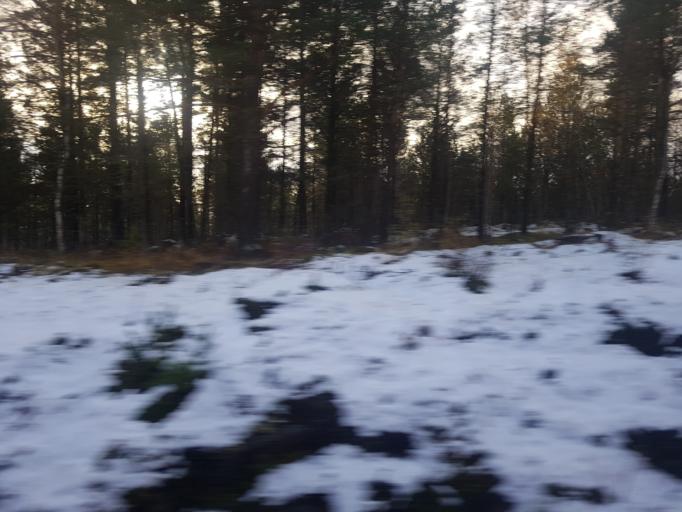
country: NO
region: Sor-Trondelag
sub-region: Oppdal
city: Oppdal
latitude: 62.6417
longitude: 9.8150
